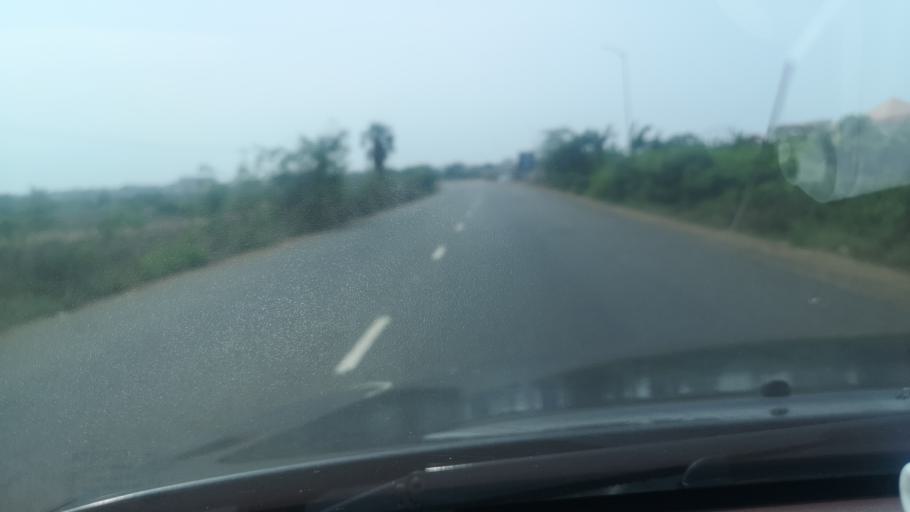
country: GH
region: Greater Accra
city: Nungua
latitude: 5.6121
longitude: -0.0547
